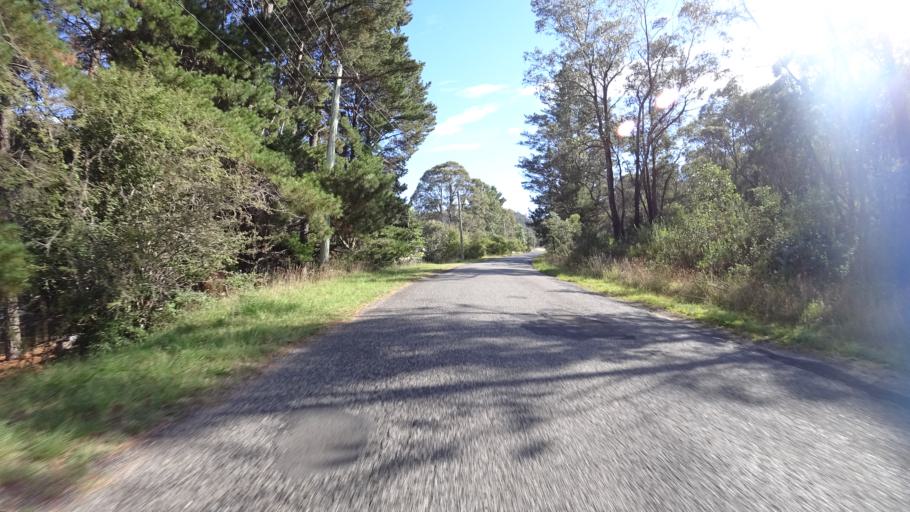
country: AU
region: New South Wales
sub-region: Lithgow
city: Lithgow
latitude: -33.4681
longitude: 150.1680
